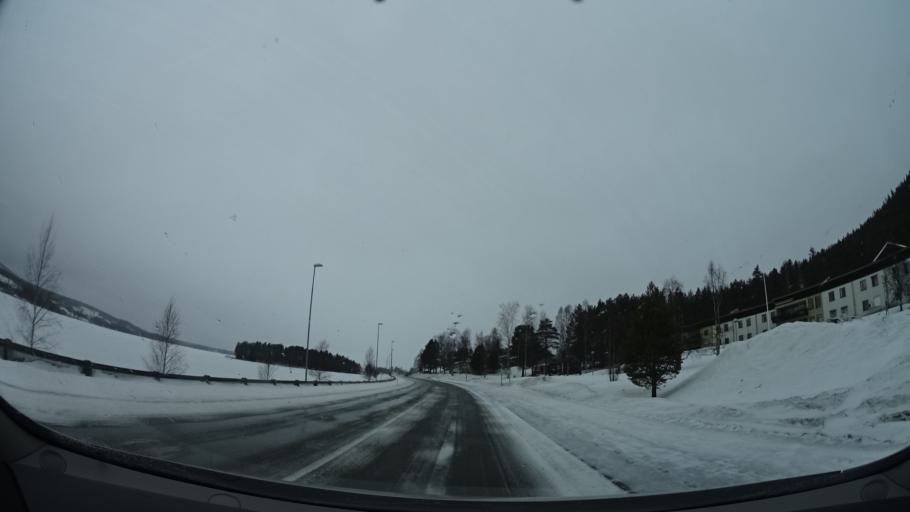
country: SE
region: Vaesterbotten
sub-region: Mala Kommun
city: Mala
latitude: 65.1746
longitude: 18.7550
